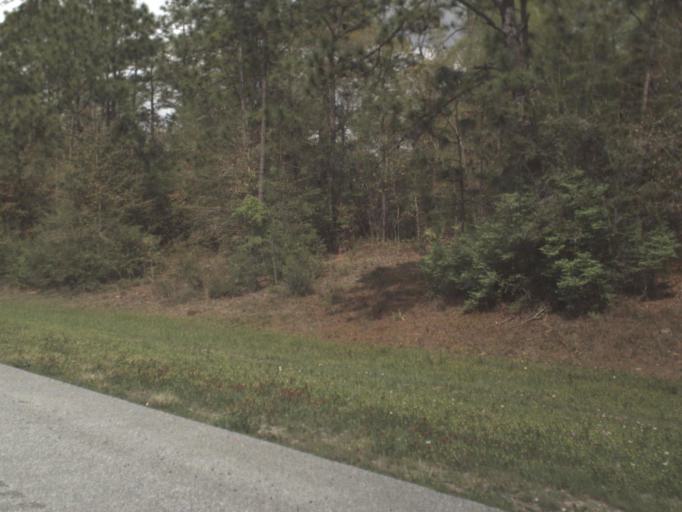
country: US
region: Florida
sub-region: Okaloosa County
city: Crestview
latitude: 30.7094
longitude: -86.7182
